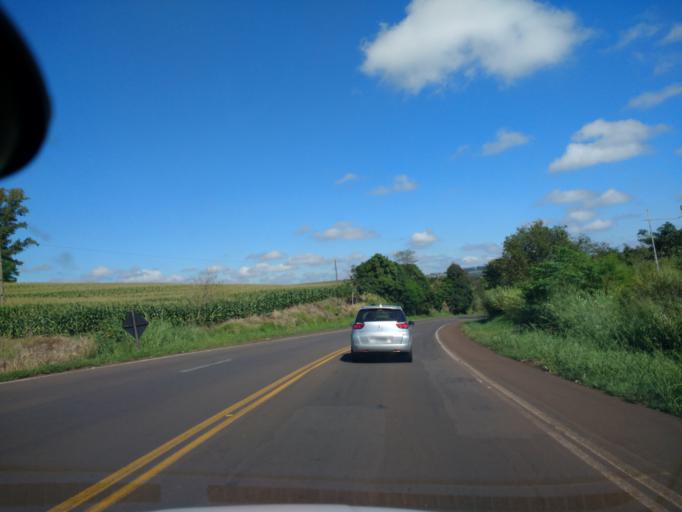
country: BR
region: Parana
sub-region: Cianorte
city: Cianorte
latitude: -23.6562
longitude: -52.5038
